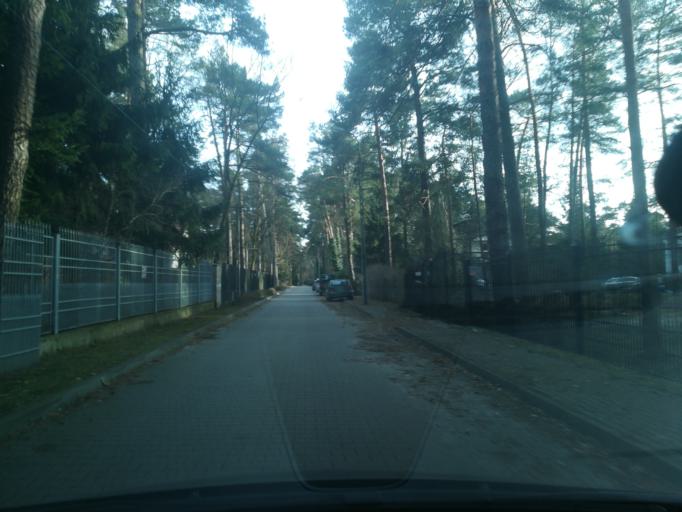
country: PL
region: Masovian Voivodeship
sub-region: Powiat piaseczynski
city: Konstancin-Jeziorna
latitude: 52.0765
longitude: 21.1075
